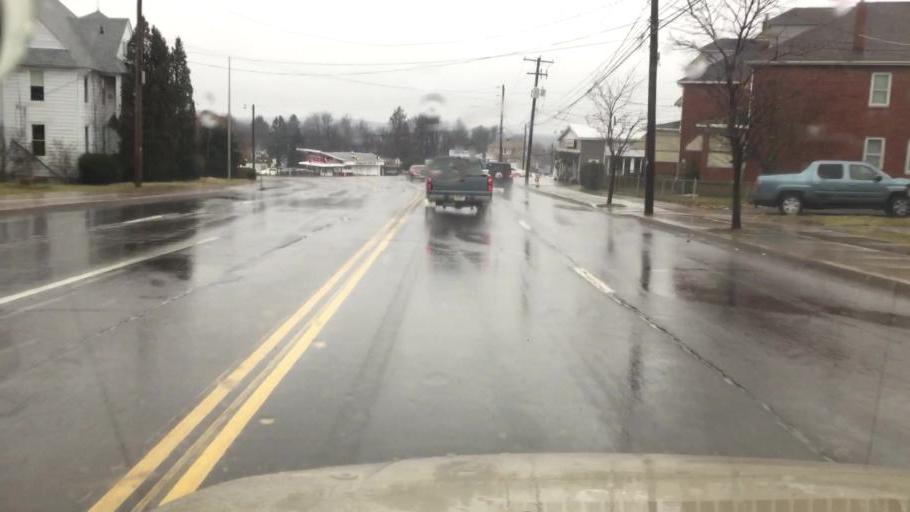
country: US
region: Pennsylvania
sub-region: Luzerne County
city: West Hazleton
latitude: 40.9655
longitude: -75.9976
